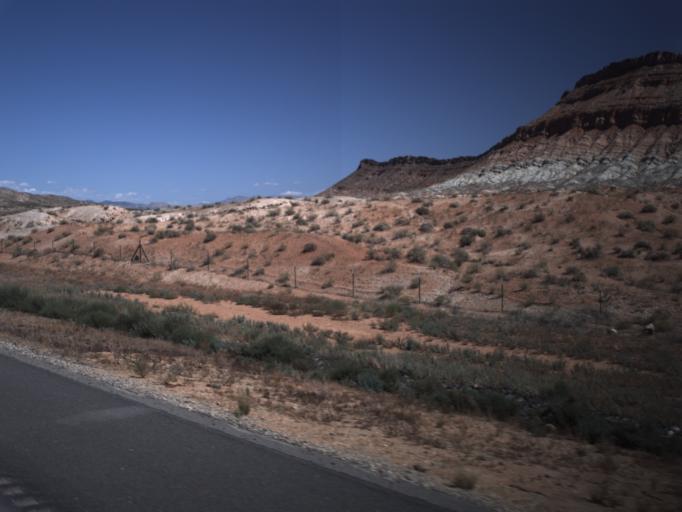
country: US
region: Utah
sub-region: Washington County
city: Washington
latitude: 37.0702
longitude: -113.4858
